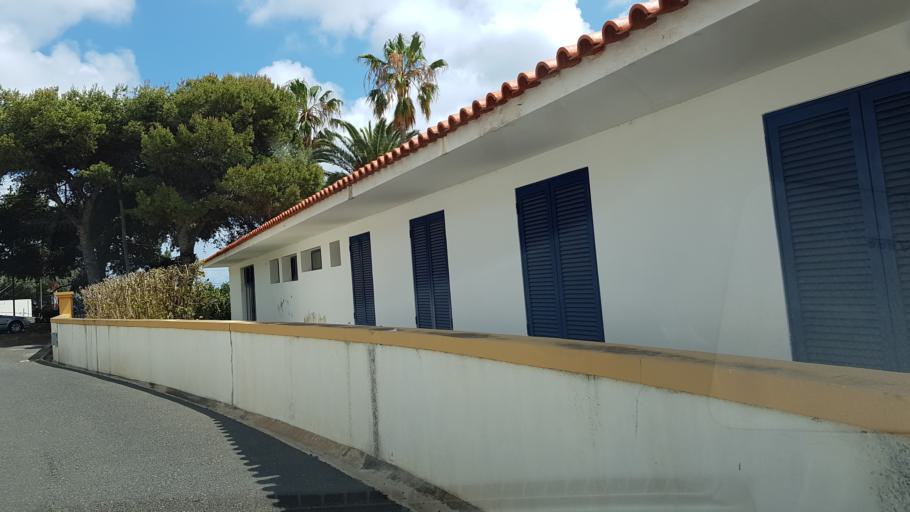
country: PT
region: Madeira
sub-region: Porto Santo
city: Vila de Porto Santo
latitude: 33.0597
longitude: -16.3394
